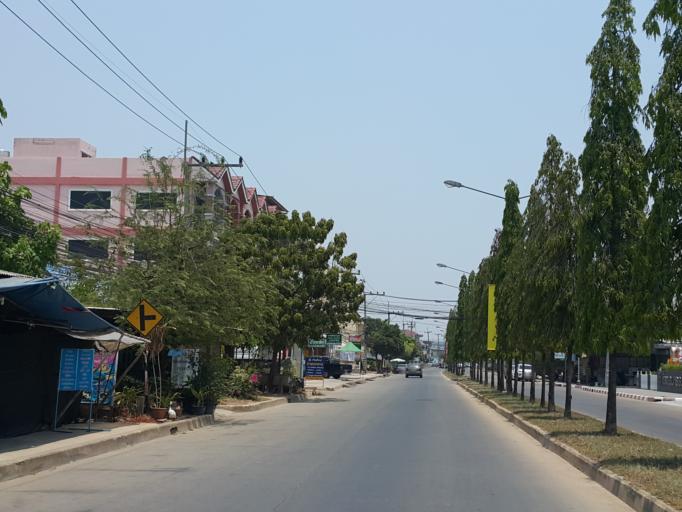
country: TH
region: Phitsanulok
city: Phitsanulok
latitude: 16.8182
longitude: 100.2453
